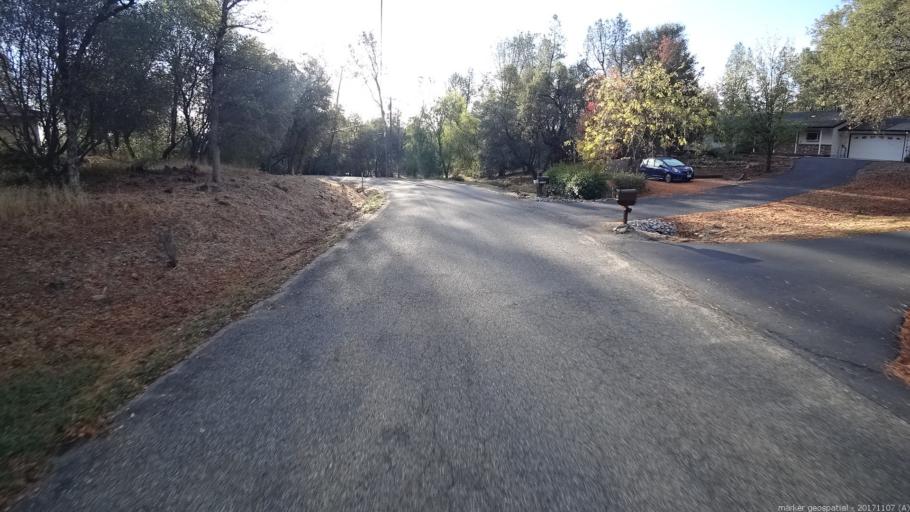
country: US
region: California
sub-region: Shasta County
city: Shasta
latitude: 40.5803
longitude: -122.4688
